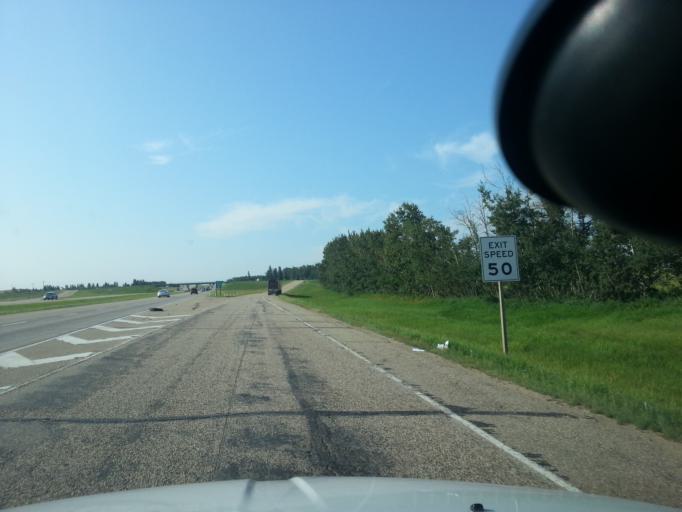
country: CA
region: Alberta
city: Ponoka
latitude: 52.8485
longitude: -113.6443
